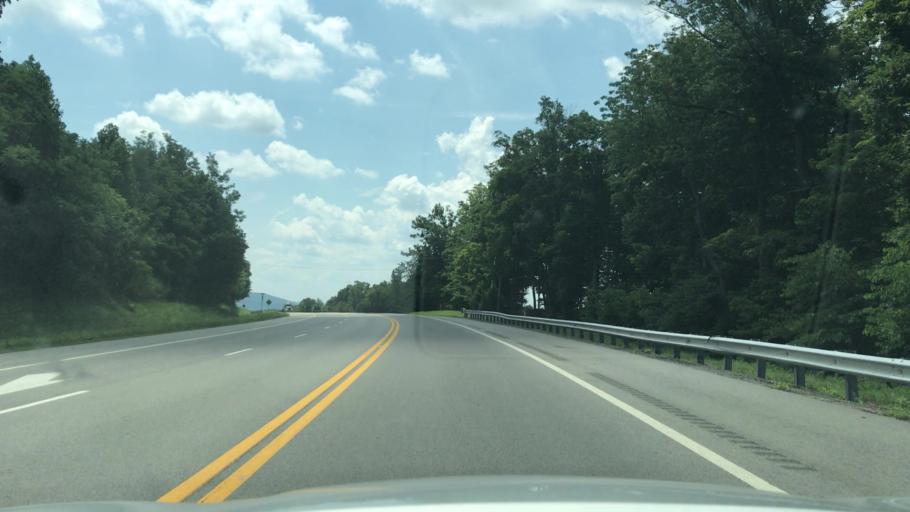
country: US
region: Tennessee
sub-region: Pickett County
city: Byrdstown
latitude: 36.5517
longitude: -85.1679
